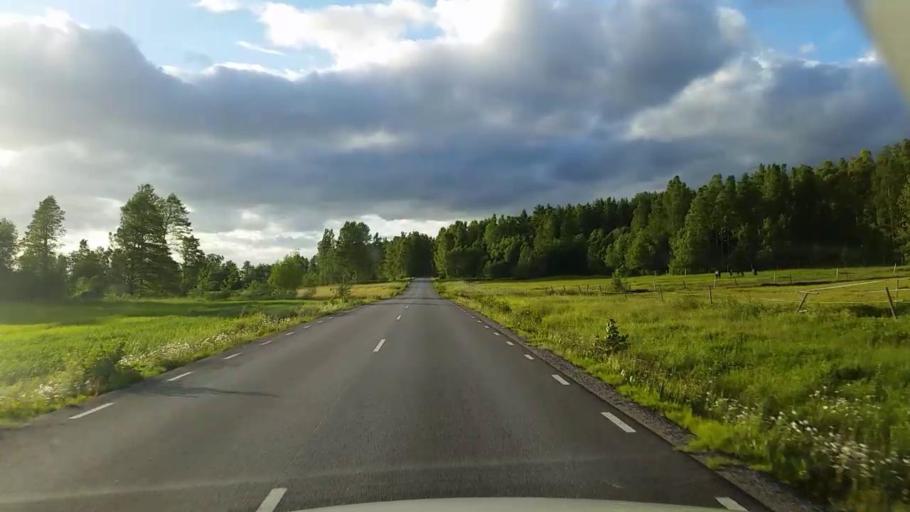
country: SE
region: Vaestmanland
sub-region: Kopings Kommun
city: Kolsva
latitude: 59.7042
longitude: 15.8301
